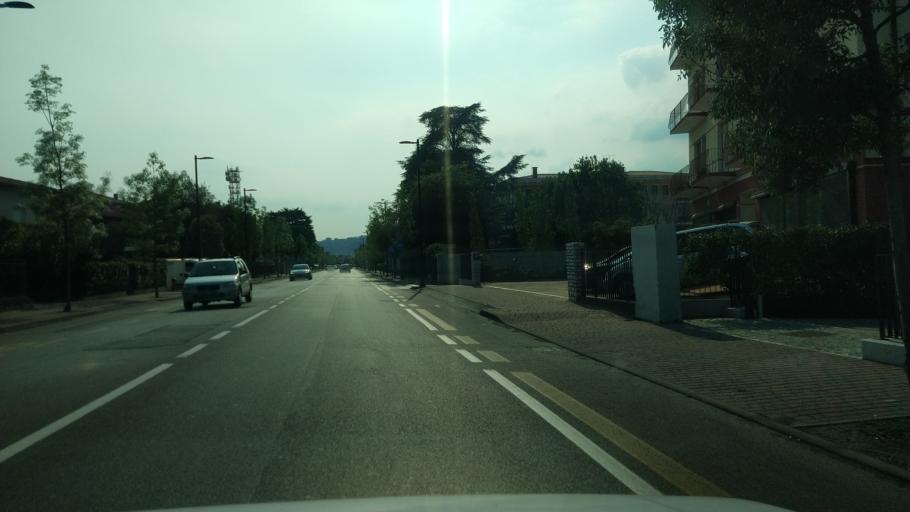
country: IT
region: Veneto
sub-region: Provincia di Vicenza
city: Bassano del Grappa
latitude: 45.7654
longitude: 11.7240
